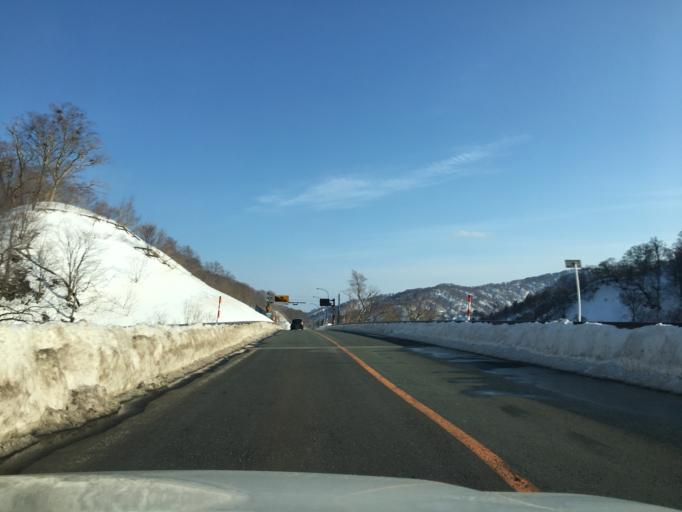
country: JP
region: Yamagata
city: Tsuruoka
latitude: 38.5237
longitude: 139.9498
